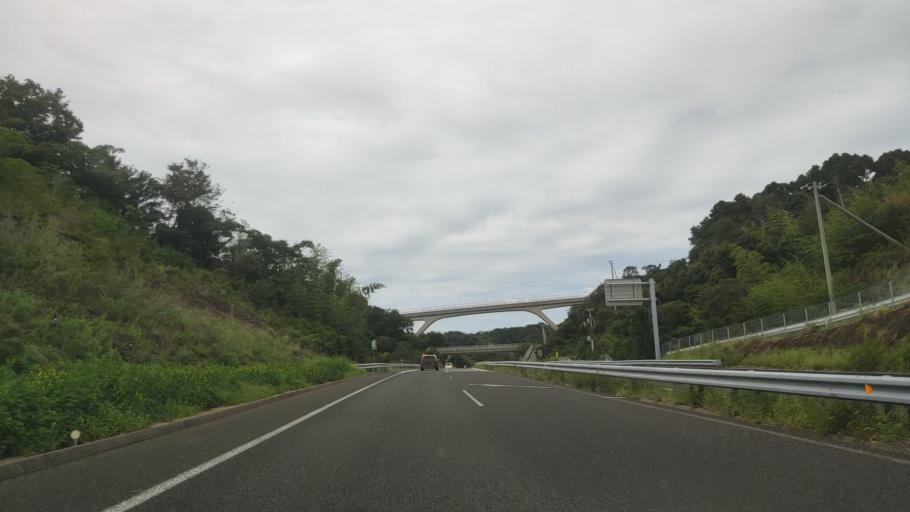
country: JP
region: Wakayama
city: Gobo
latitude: 33.8130
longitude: 135.2327
